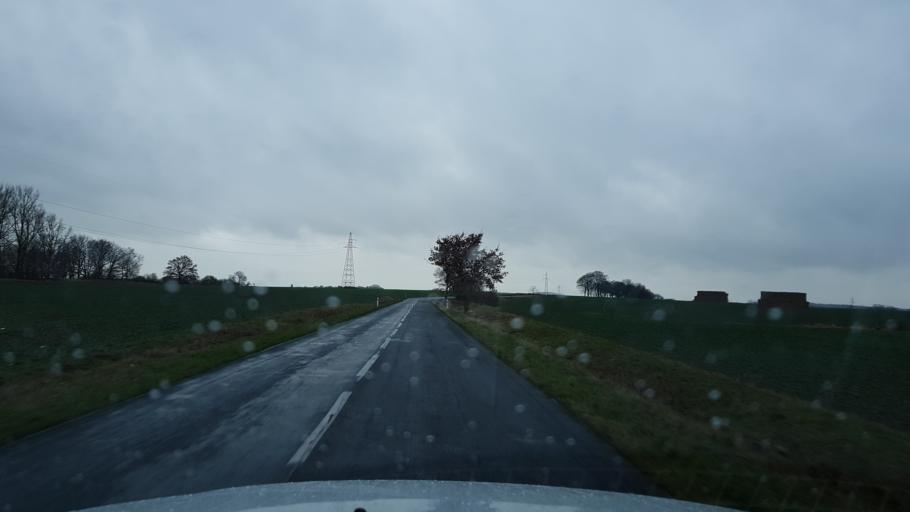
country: PL
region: West Pomeranian Voivodeship
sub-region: Powiat lobeski
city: Radowo Male
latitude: 53.5987
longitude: 15.4200
